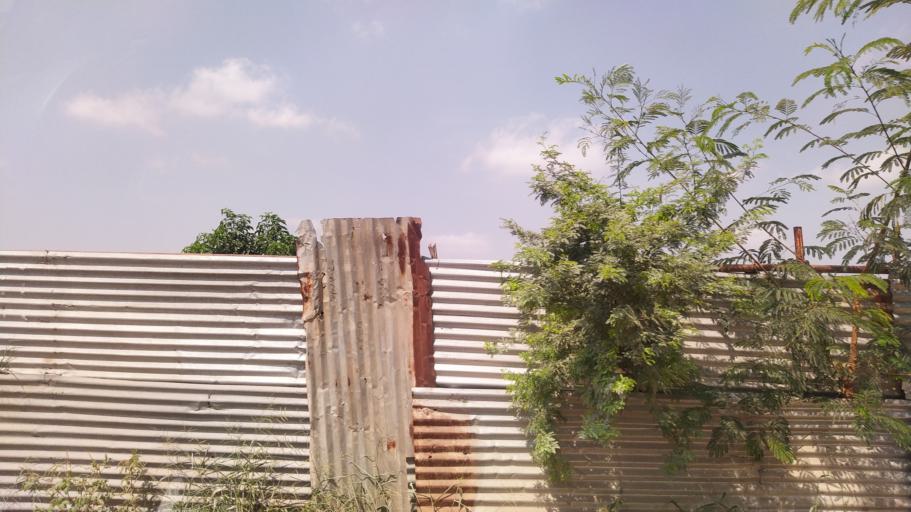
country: AO
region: Luanda
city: Luanda
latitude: -8.9064
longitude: 13.2335
